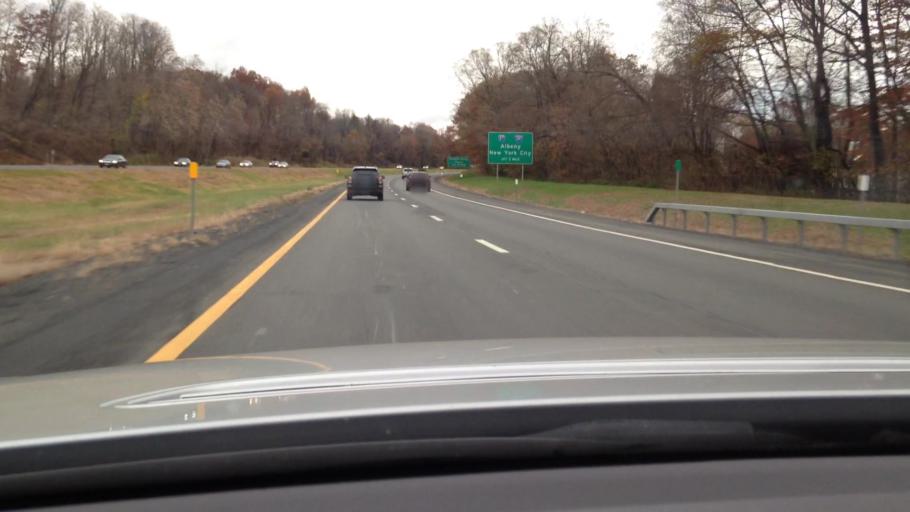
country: US
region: New York
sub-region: Rockland County
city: Chestnut Ridge
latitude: 41.0778
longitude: -74.0499
